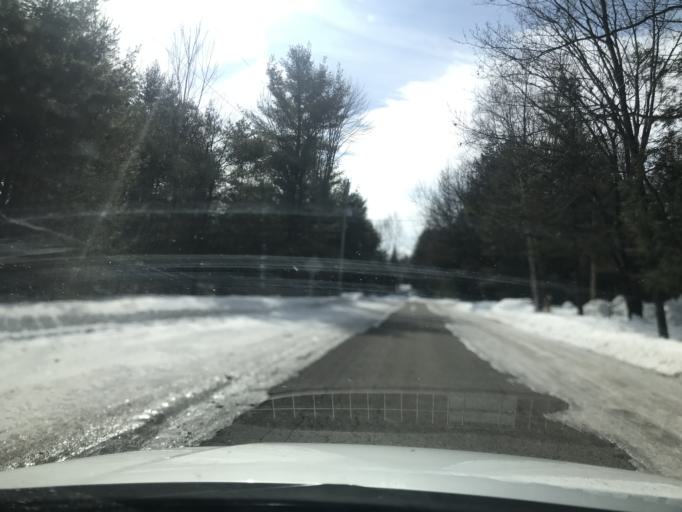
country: US
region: Wisconsin
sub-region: Menominee County
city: Legend Lake
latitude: 45.1071
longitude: -88.4331
